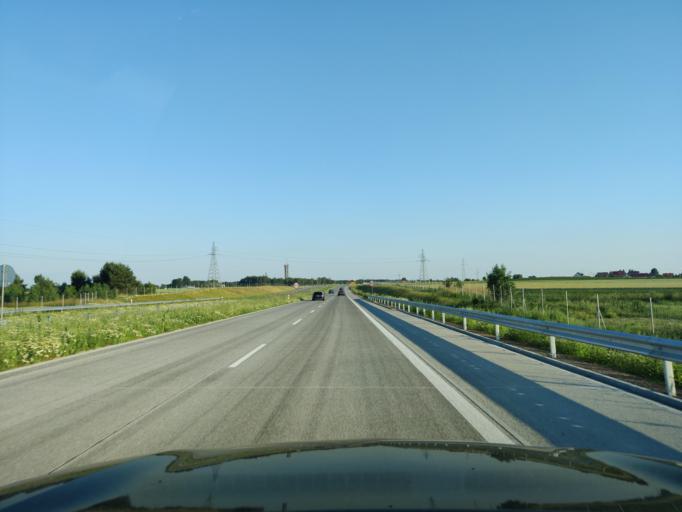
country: PL
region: Masovian Voivodeship
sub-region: Powiat mlawski
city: Mlawa
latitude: 53.1097
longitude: 20.4111
